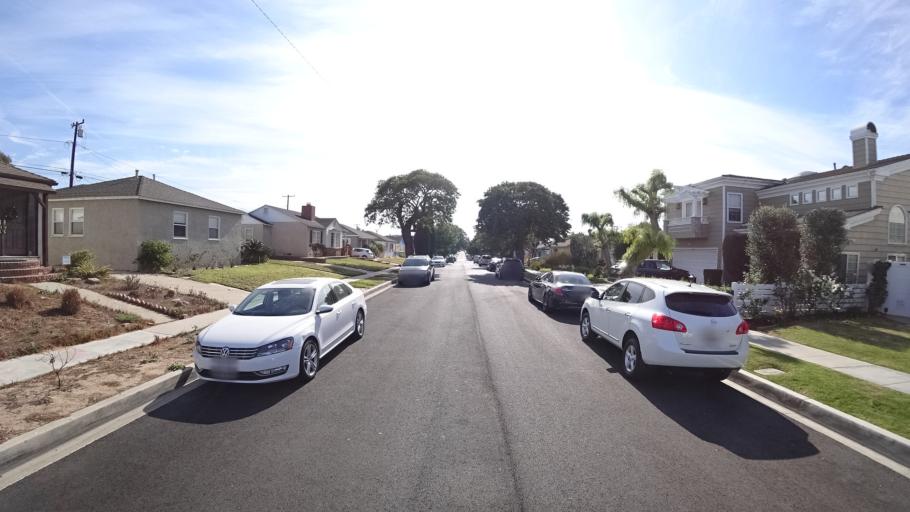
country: US
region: California
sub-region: Los Angeles County
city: Del Aire
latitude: 33.8931
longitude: -118.3826
